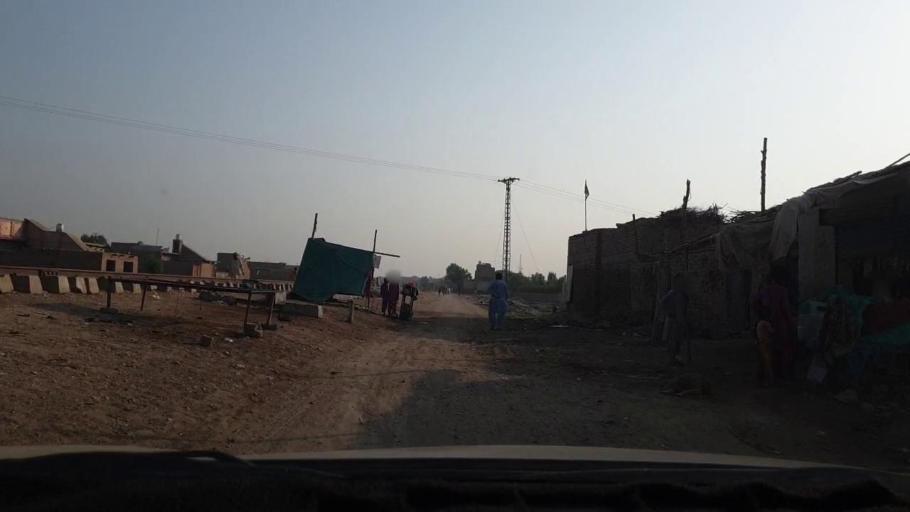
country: PK
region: Sindh
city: Larkana
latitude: 27.5339
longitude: 68.2027
